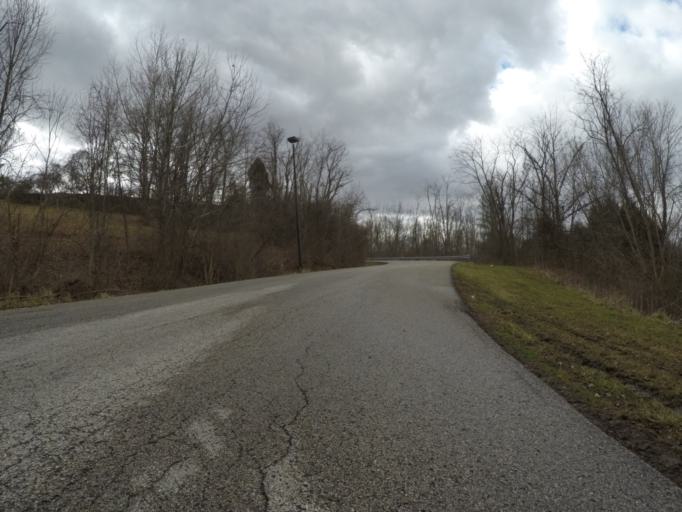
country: US
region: West Virginia
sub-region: Cabell County
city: Pea Ridge
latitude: 38.4042
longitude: -82.3738
